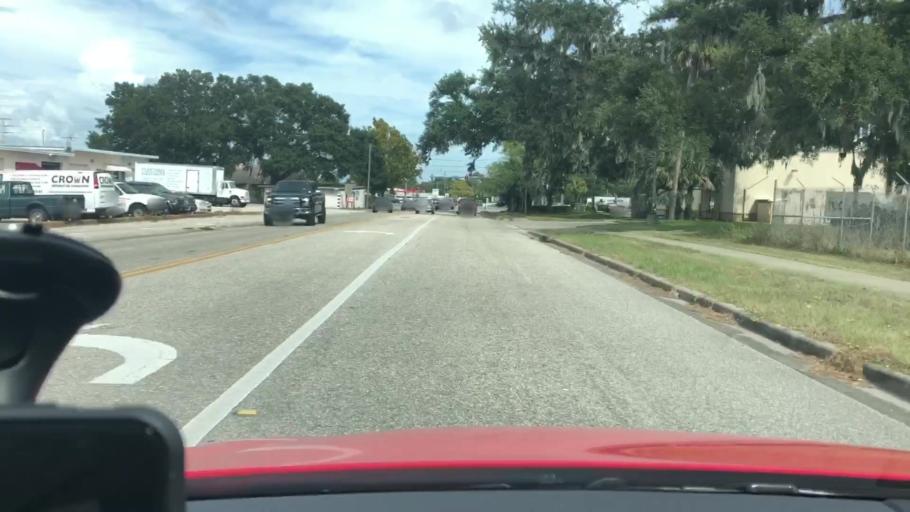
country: US
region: Florida
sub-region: Volusia County
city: South Daytona
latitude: 29.1537
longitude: -81.0213
